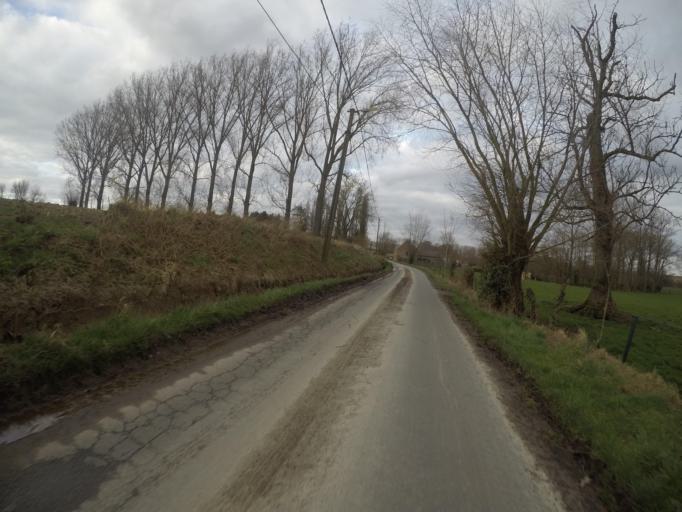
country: BE
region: Flanders
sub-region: Provincie Vlaams-Brabant
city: Pepingen
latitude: 50.7520
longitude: 4.1374
